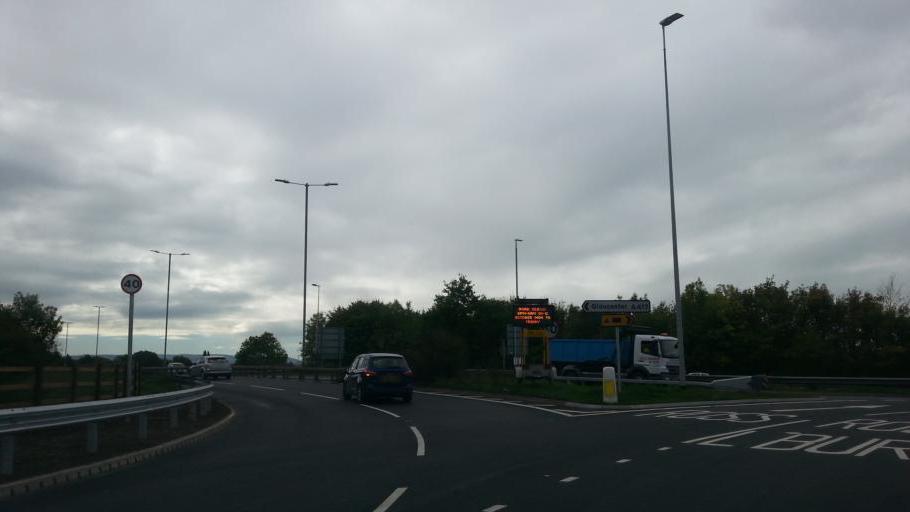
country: GB
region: England
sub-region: Gloucestershire
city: Gloucester
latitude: 51.8752
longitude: -2.2644
